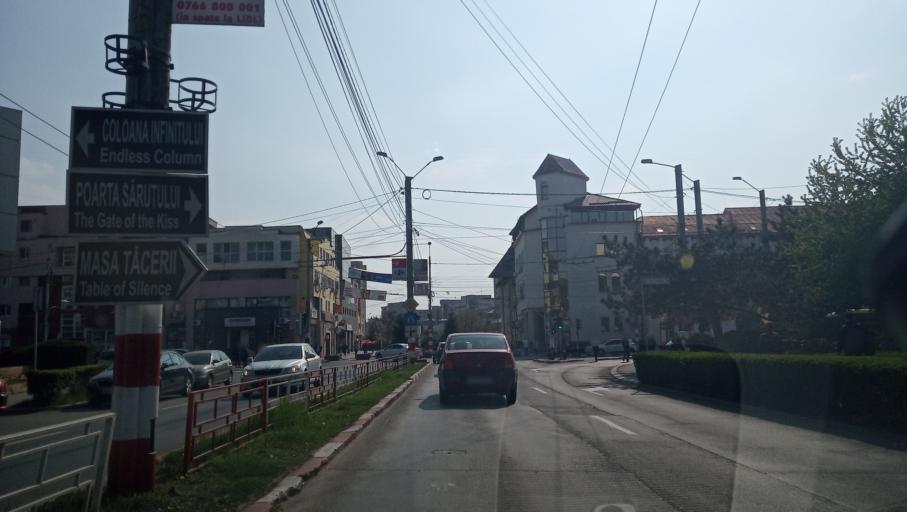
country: RO
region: Gorj
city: Targu Jiu
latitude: 45.0418
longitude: 23.2737
